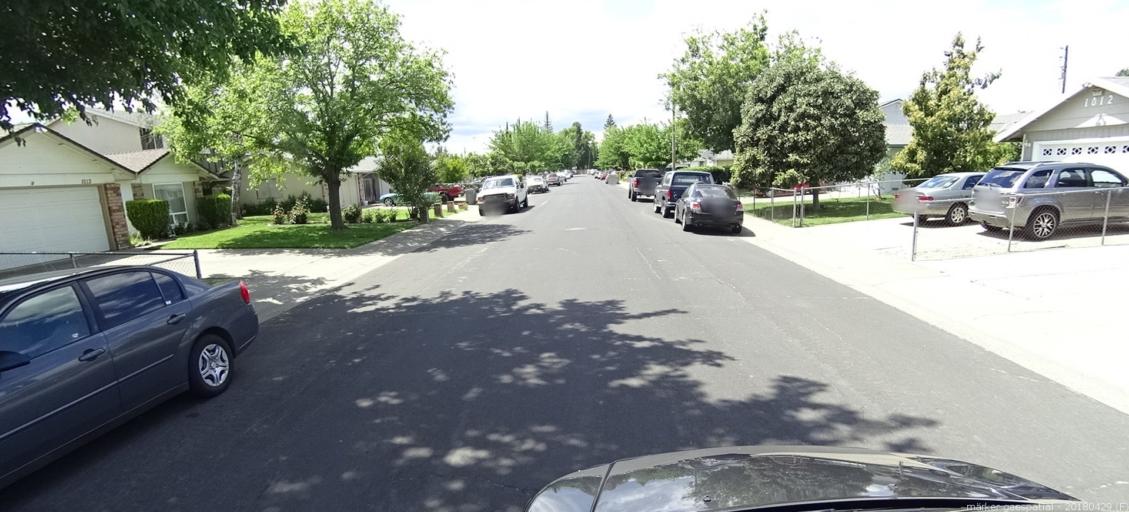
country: US
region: California
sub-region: Yolo County
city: West Sacramento
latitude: 38.5970
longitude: -121.5272
